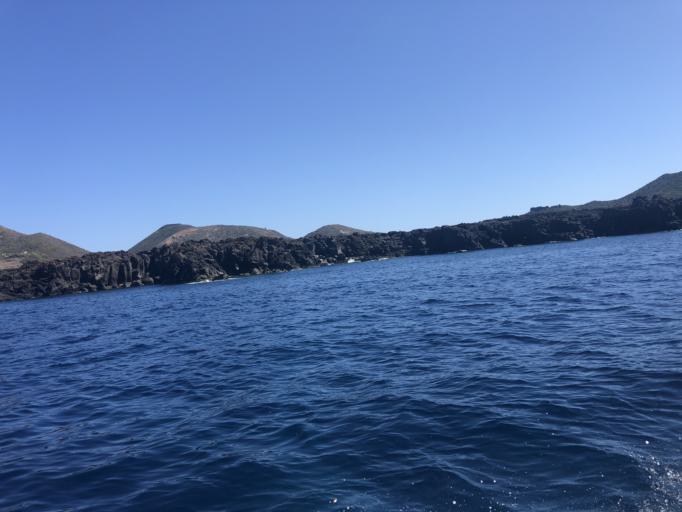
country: IT
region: Sicily
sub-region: Agrigento
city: Lampedusa
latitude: 35.8765
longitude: 12.8593
